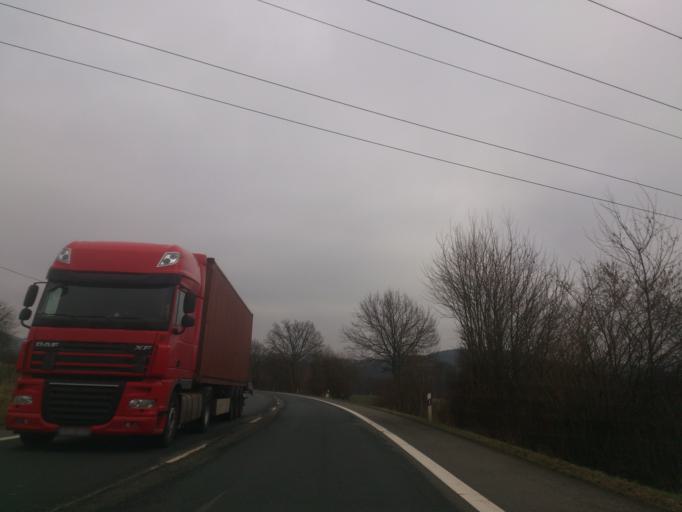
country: DE
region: North Rhine-Westphalia
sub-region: Regierungsbezirk Detmold
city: Vlotho
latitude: 52.1419
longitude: 8.8185
